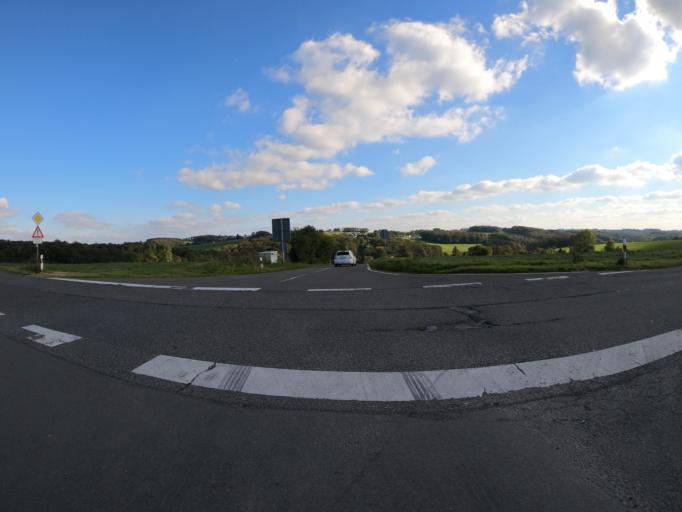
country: DE
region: North Rhine-Westphalia
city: Radevormwald
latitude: 51.2289
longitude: 7.3411
